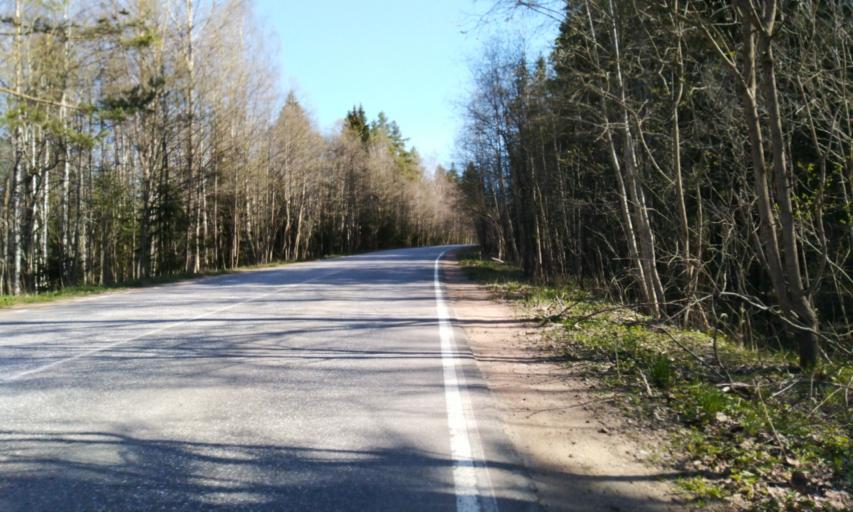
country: RU
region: Leningrad
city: Garbolovo
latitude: 60.3446
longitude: 30.4383
